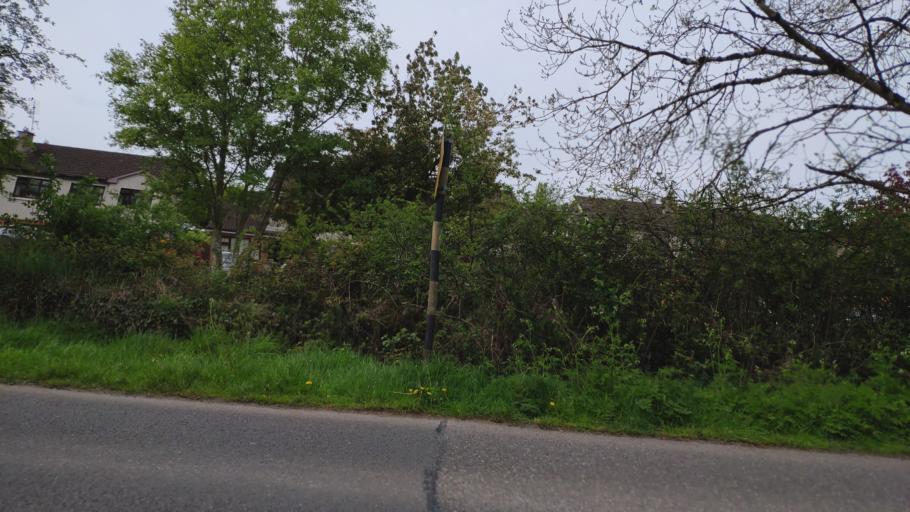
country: IE
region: Munster
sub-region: County Cork
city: Cork
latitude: 51.9220
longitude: -8.4557
